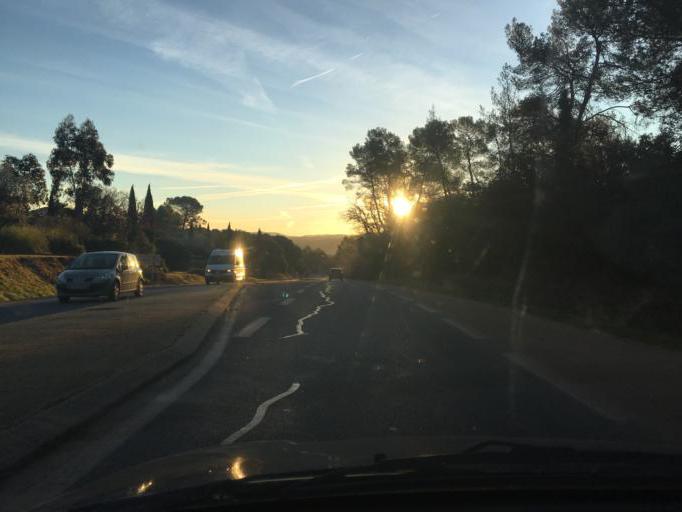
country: FR
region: Provence-Alpes-Cote d'Azur
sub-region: Departement du Var
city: Taradeau
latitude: 43.4501
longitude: 6.4326
